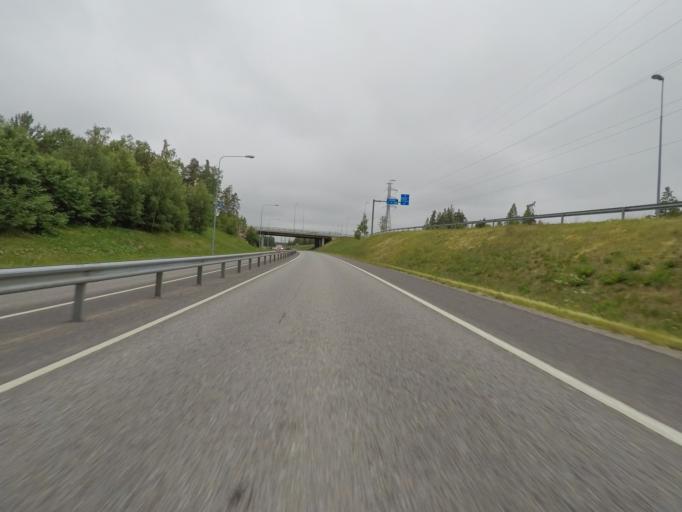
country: FI
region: Varsinais-Suomi
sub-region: Turku
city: Naantali
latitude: 60.4735
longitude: 22.0697
